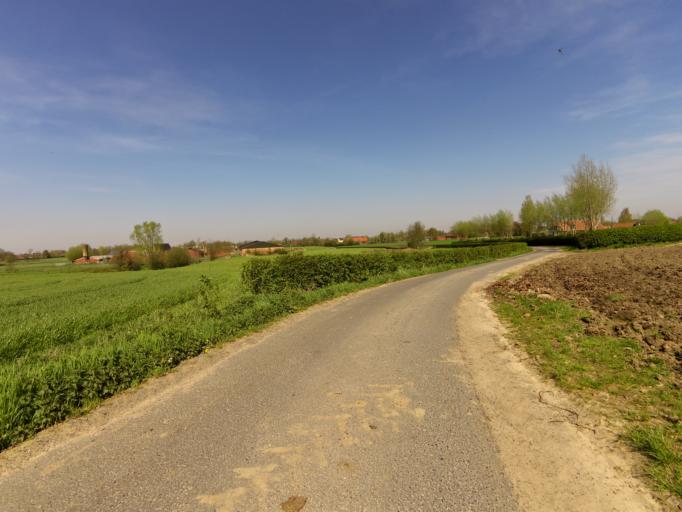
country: BE
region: Flanders
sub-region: Provincie West-Vlaanderen
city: Ichtegem
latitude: 51.0848
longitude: 2.9984
